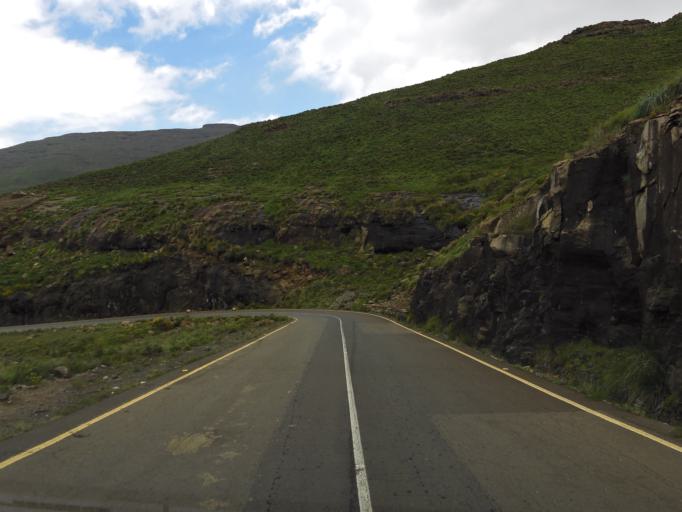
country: LS
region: Butha-Buthe
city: Butha-Buthe
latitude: -29.1142
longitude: 28.4396
